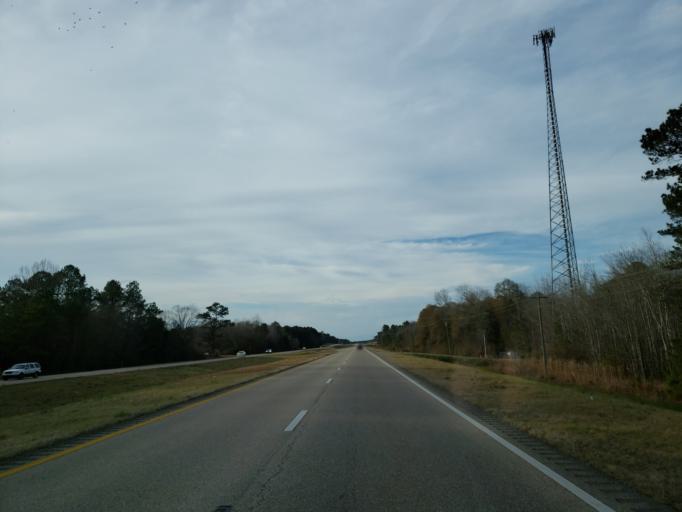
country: US
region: Mississippi
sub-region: Wayne County
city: Waynesboro
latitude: 31.6132
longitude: -88.5716
